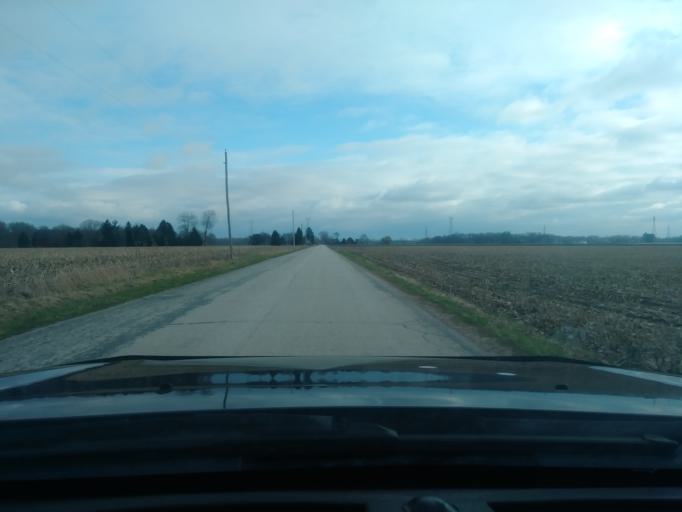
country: US
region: Indiana
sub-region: LaPorte County
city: LaPorte
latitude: 41.5600
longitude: -86.7984
